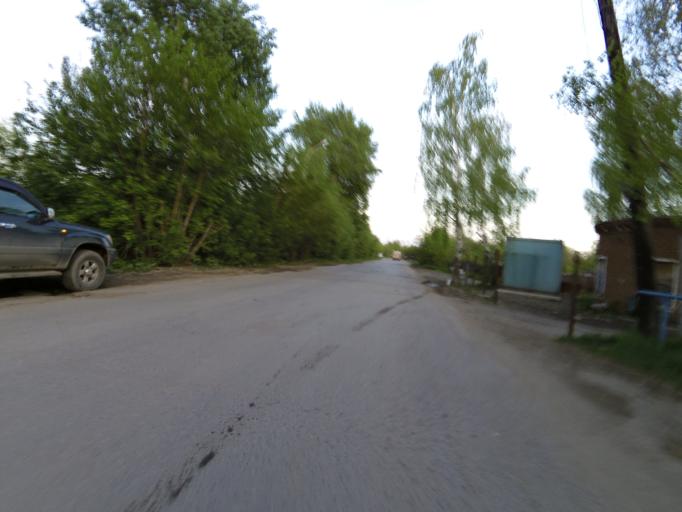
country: RU
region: Sverdlovsk
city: Shirokaya Rechka
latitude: 56.8458
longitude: 60.4979
